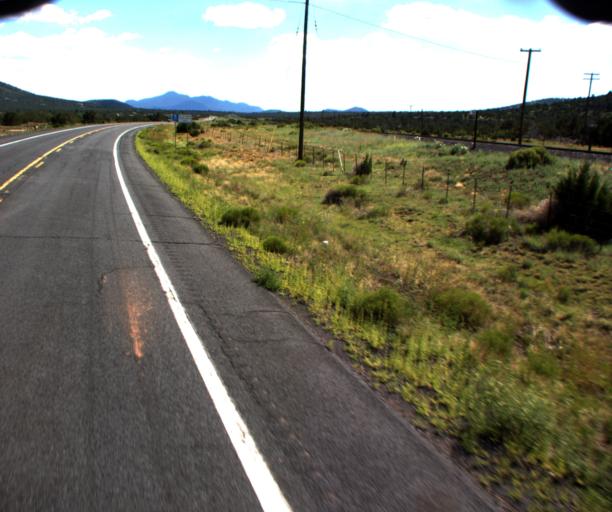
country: US
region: Arizona
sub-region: Coconino County
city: Williams
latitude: 35.3780
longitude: -112.1616
